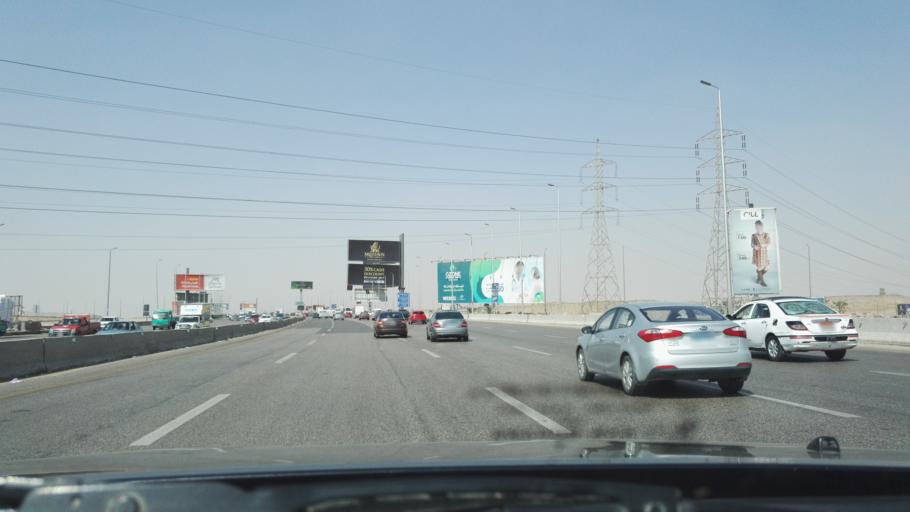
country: EG
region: Muhafazat al Qalyubiyah
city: Al Khankah
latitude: 30.0772
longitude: 31.4343
